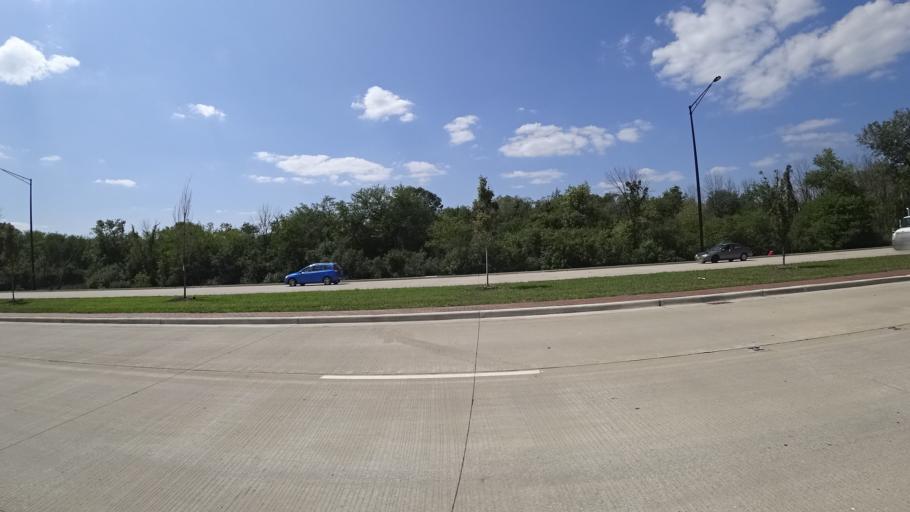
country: US
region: Illinois
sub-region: Cook County
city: Orland Park
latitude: 41.6395
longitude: -87.8537
